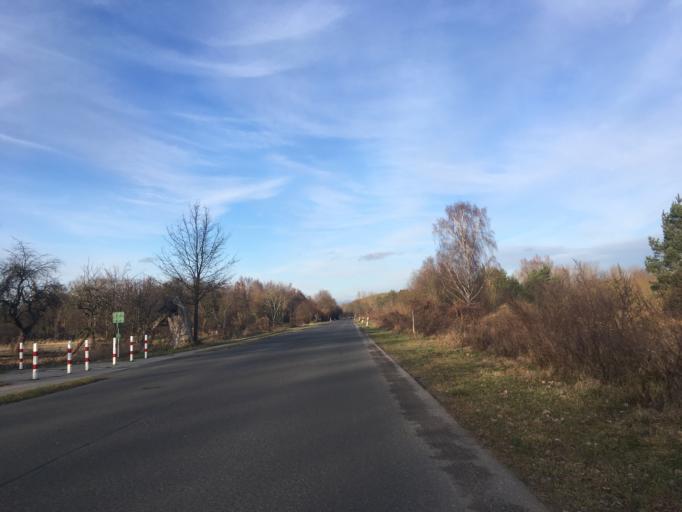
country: DE
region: Berlin
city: Blankenfelde
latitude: 52.6238
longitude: 13.3992
